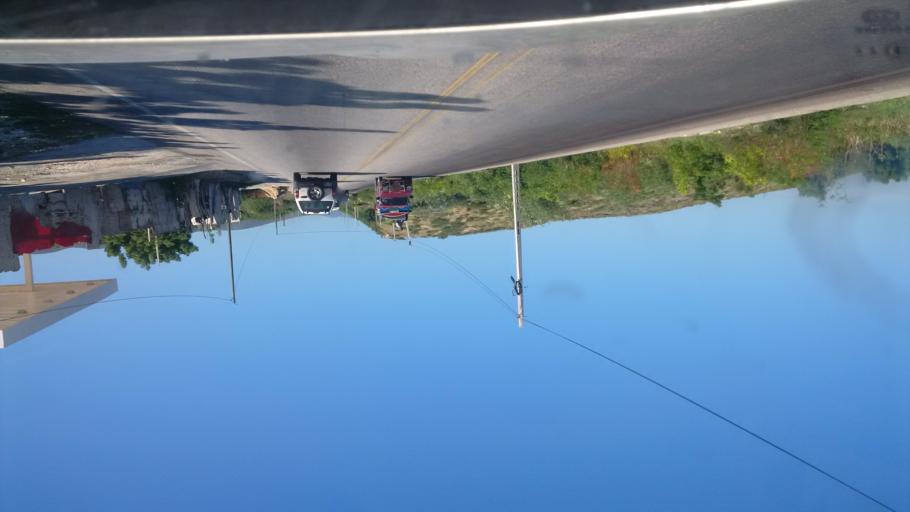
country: HT
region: Ouest
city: Cabaret
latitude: 18.6852
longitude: -72.3333
